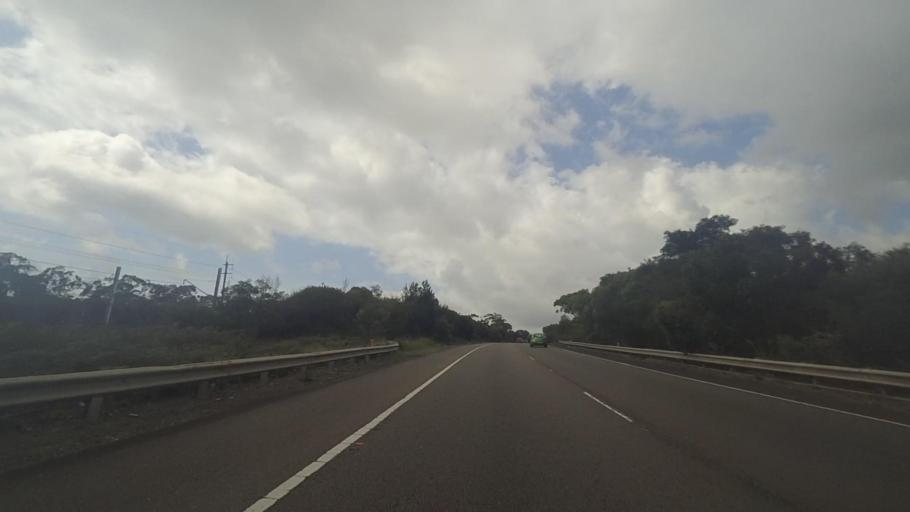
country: AU
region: New South Wales
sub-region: Sutherland Shire
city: Heathcote
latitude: -34.1099
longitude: 150.9934
